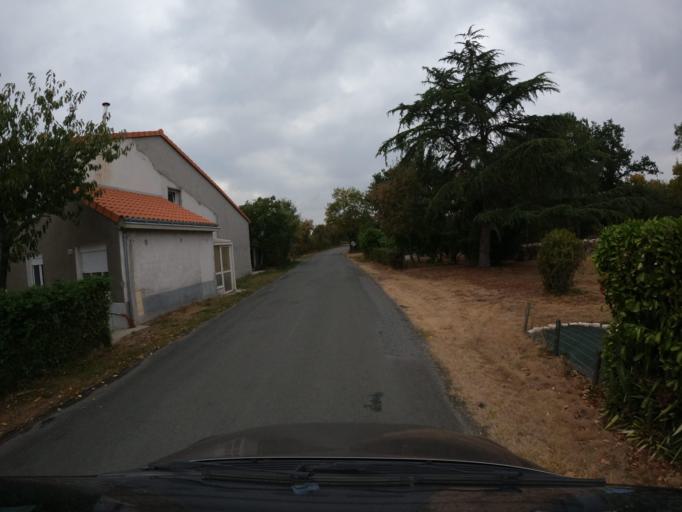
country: FR
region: Pays de la Loire
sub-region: Departement de la Vendee
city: Montaigu
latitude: 46.9743
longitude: -1.2889
